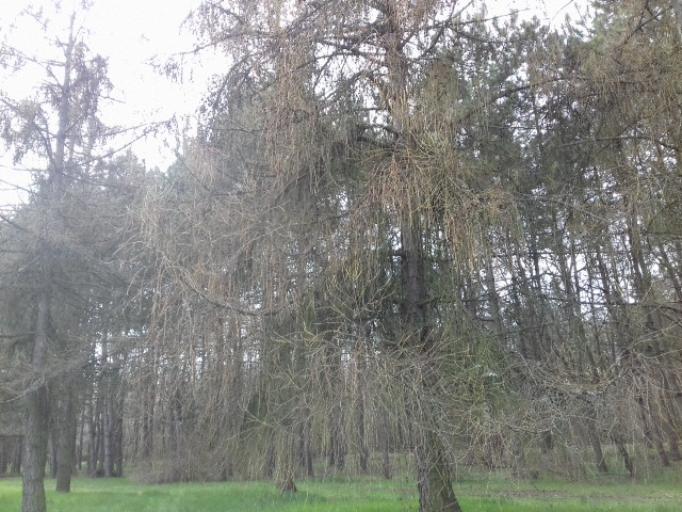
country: HU
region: Bacs-Kiskun
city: Tiszakecske
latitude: 46.8919
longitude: 20.1222
